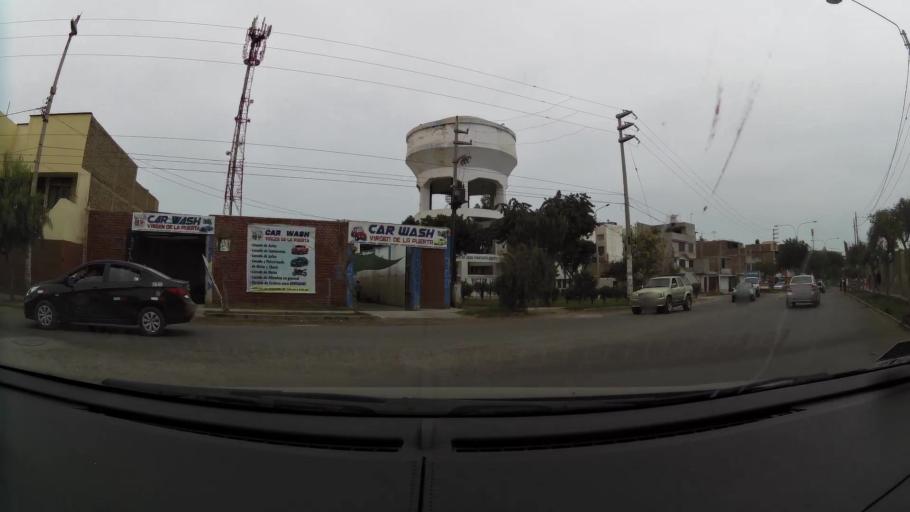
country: PE
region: La Libertad
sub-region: Provincia de Trujillo
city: Buenos Aires
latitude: -8.1361
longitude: -79.0414
